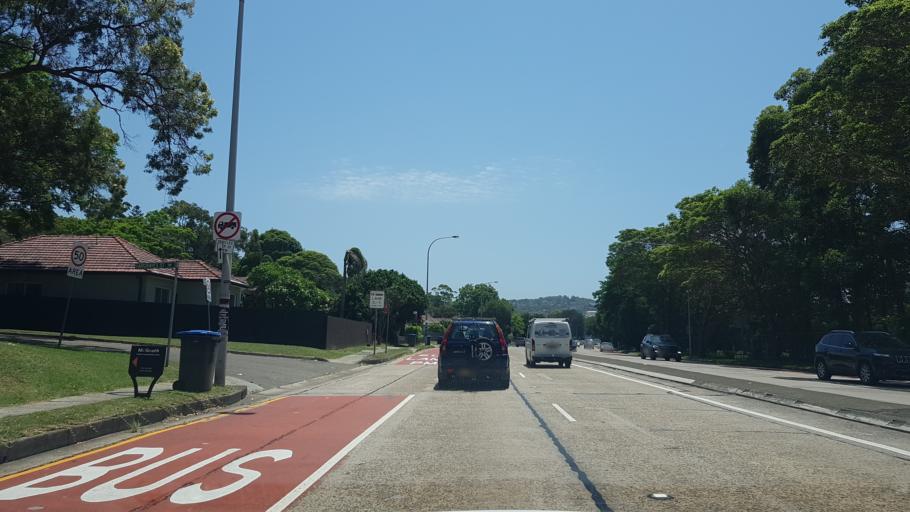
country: AU
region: New South Wales
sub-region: Warringah
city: North Manly
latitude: -33.7742
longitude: 151.2661
